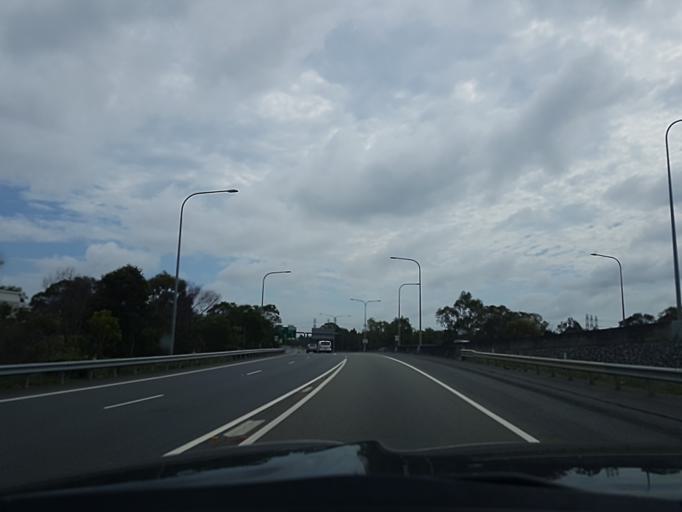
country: AU
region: Queensland
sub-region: Brisbane
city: Cannon Hill
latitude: -27.4563
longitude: 153.1103
